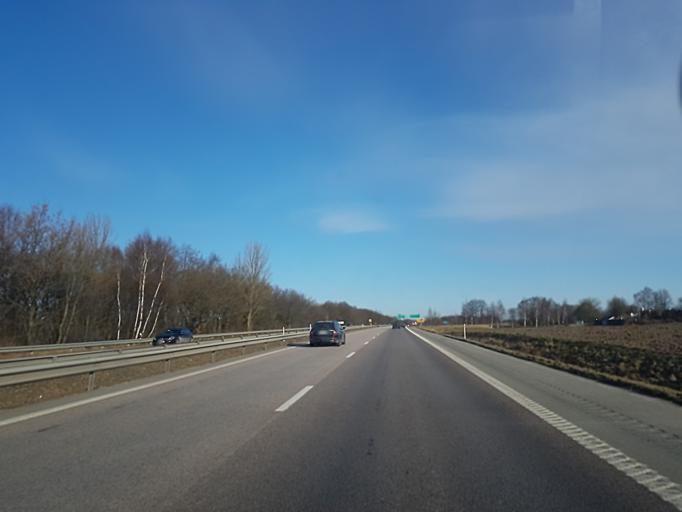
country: SE
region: Skane
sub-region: Helsingborg
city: Gantofta
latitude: 56.0070
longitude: 12.7801
